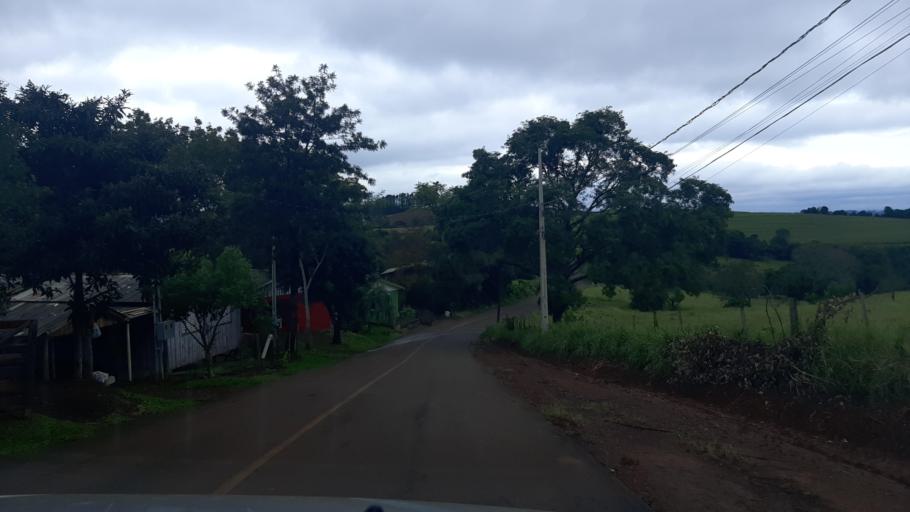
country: BR
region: Parana
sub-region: Ampere
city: Ampere
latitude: -26.0368
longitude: -53.4882
